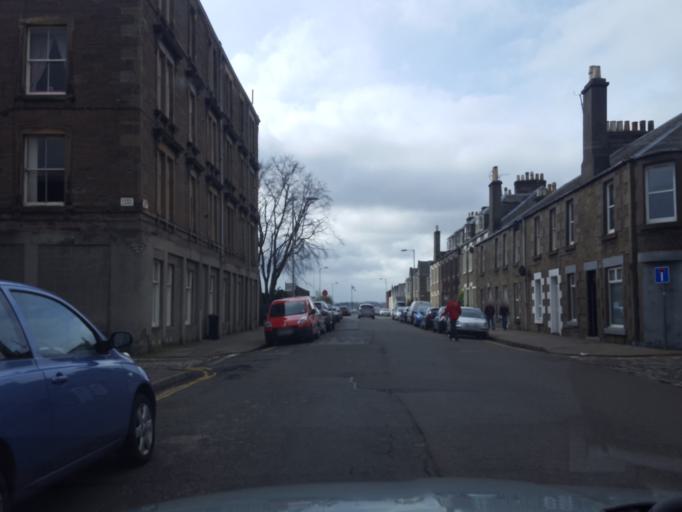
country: GB
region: Scotland
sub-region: Fife
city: Tayport
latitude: 56.4660
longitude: -2.8701
